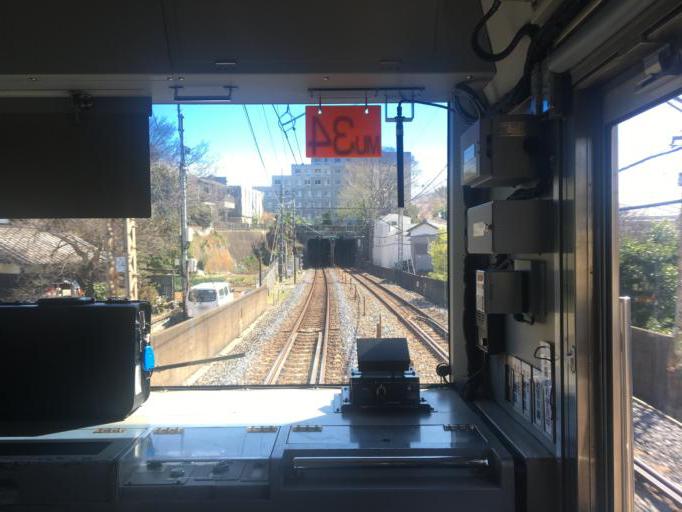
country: JP
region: Saitama
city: Yono
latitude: 35.8456
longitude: 139.6546
